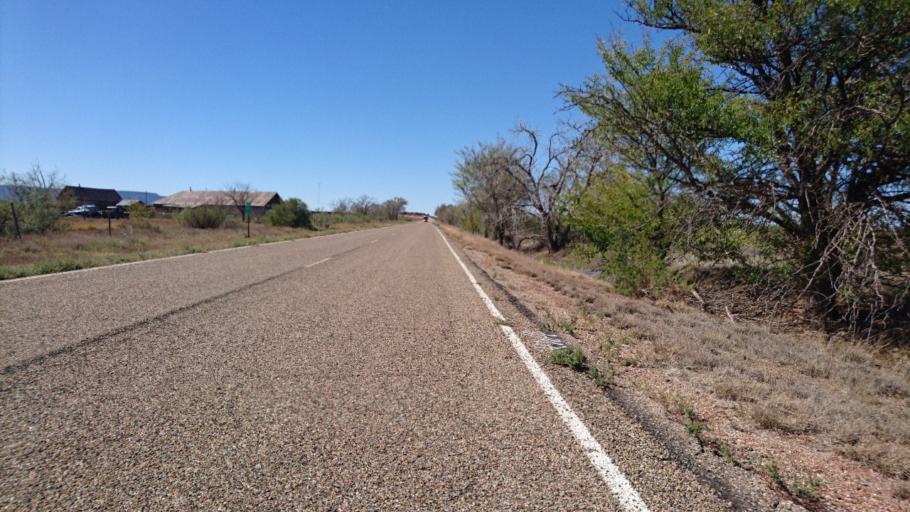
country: US
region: New Mexico
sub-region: Quay County
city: Tucumcari
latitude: 35.0968
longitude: -104.0621
